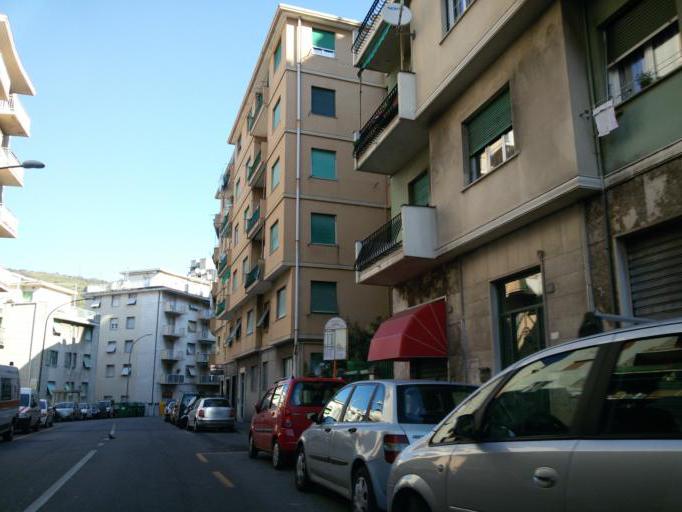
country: IT
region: Liguria
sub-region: Provincia di Genova
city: Genoa
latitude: 44.4224
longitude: 8.9203
